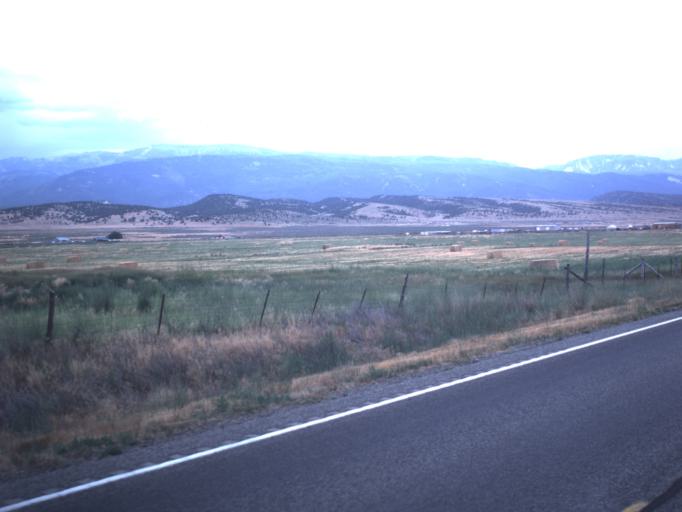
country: US
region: Utah
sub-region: Sanpete County
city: Moroni
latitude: 39.4684
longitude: -111.5628
